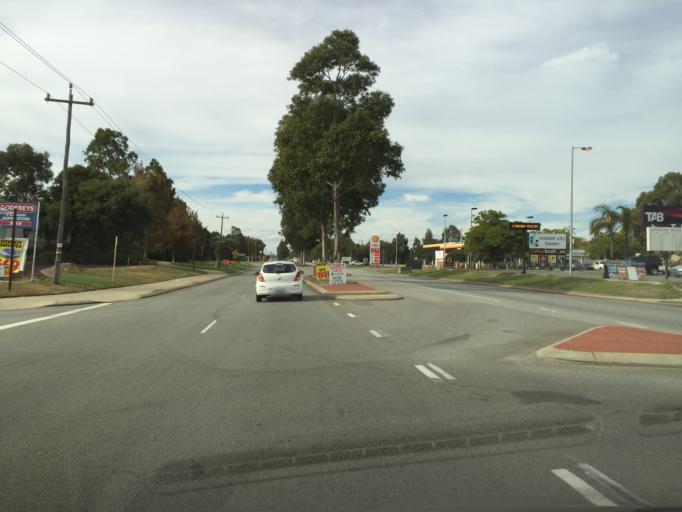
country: AU
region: Western Australia
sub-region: Canning
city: Willetton
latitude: -32.0710
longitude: 115.8941
